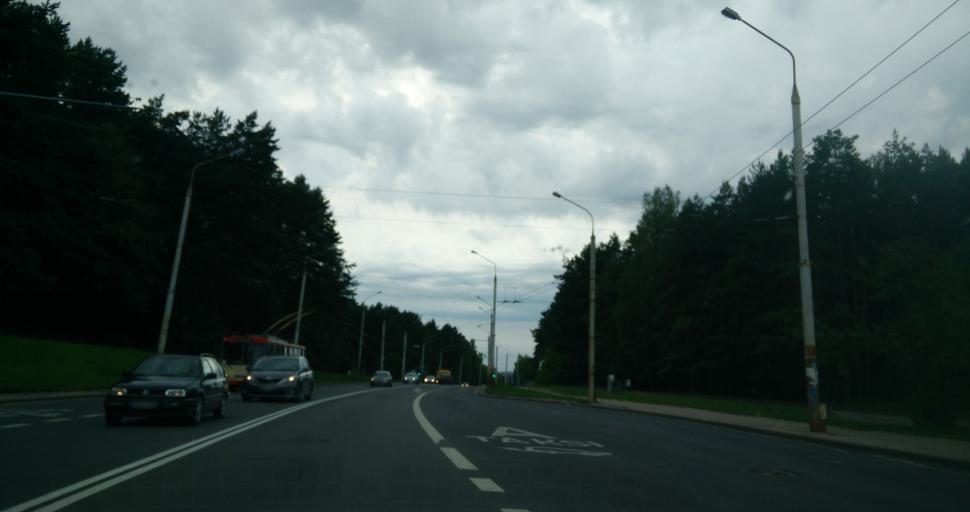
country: LT
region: Vilnius County
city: Rasos
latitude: 54.7240
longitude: 25.3348
